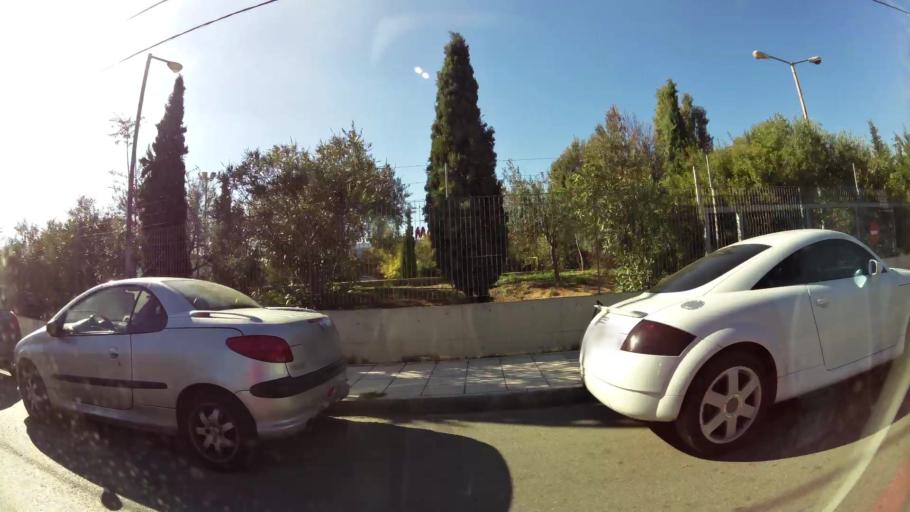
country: GR
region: Attica
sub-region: Nomarchia Anatolikis Attikis
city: Pallini
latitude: 38.0088
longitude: 23.8727
